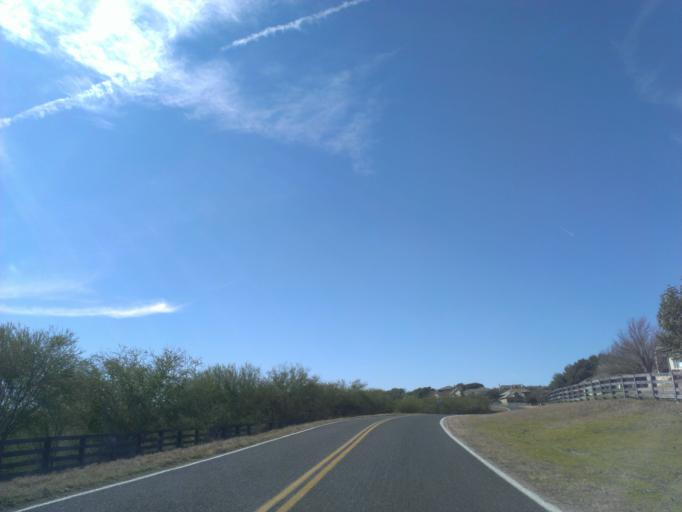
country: US
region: Texas
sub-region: Travis County
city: Briarcliff
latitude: 30.4581
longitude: -98.0987
